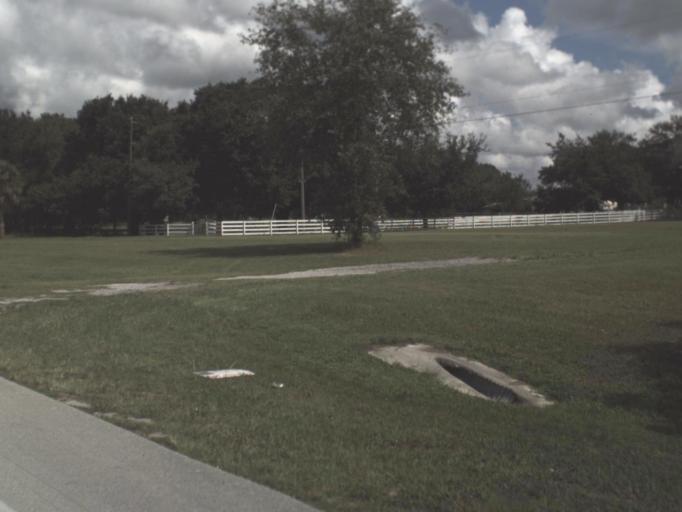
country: US
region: Florida
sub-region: Polk County
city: Polk City
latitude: 28.2914
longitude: -81.8324
